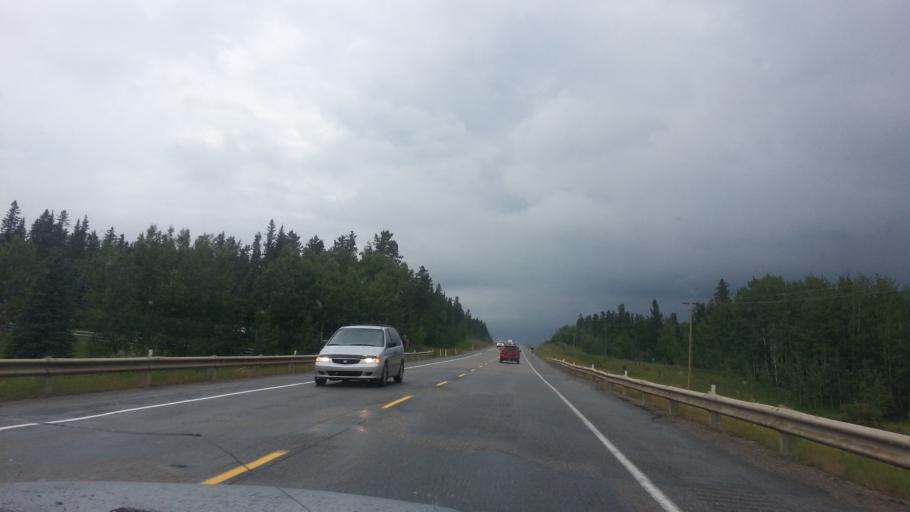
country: CA
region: Alberta
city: Cochrane
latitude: 50.9272
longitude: -114.5601
